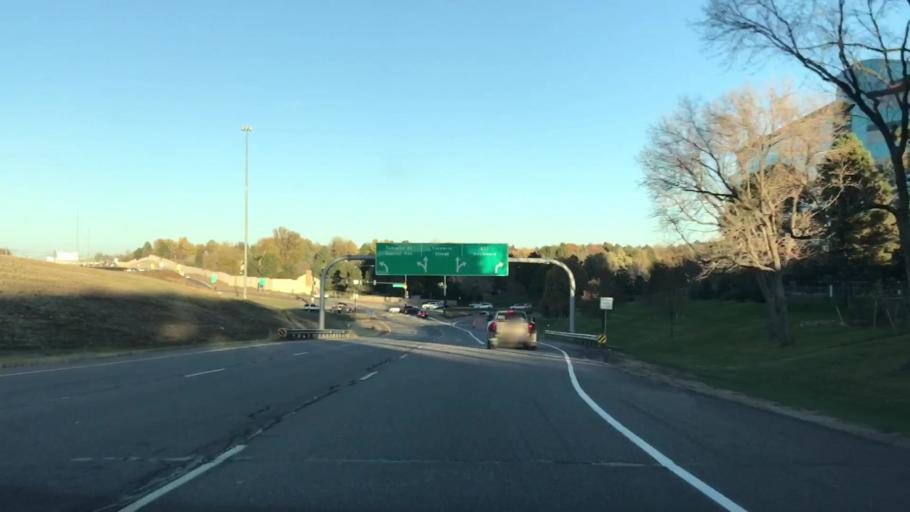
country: US
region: Colorado
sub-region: Arapahoe County
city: Castlewood
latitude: 39.6345
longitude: -104.8957
